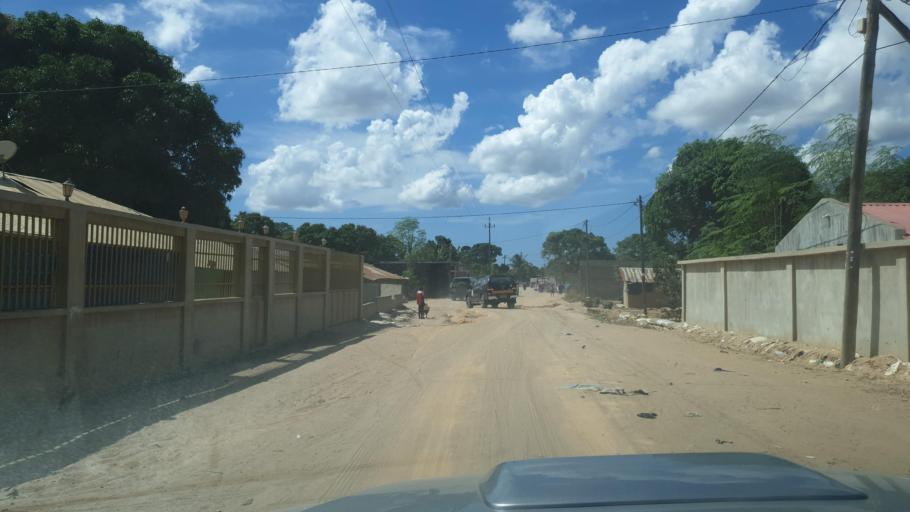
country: MZ
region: Nampula
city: Nacala
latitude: -14.5660
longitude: 40.6994
